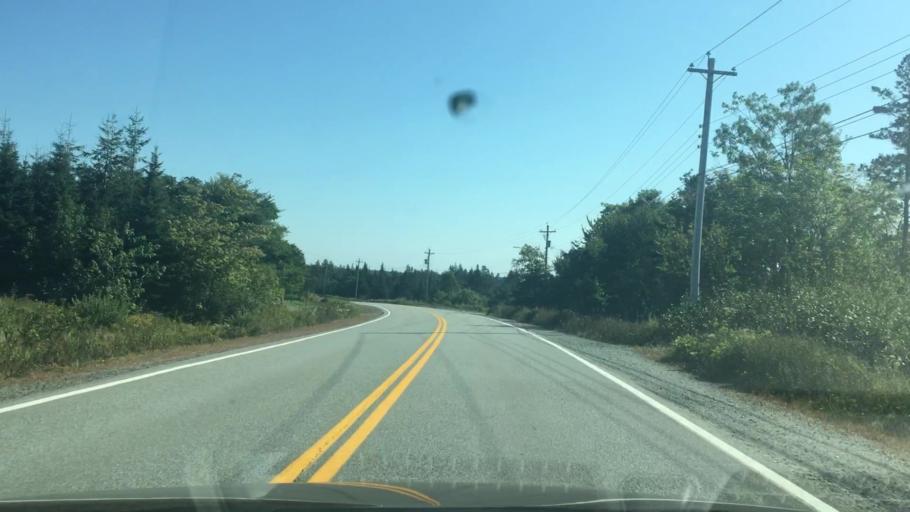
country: CA
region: Nova Scotia
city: Cole Harbour
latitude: 44.7792
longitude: -62.7761
